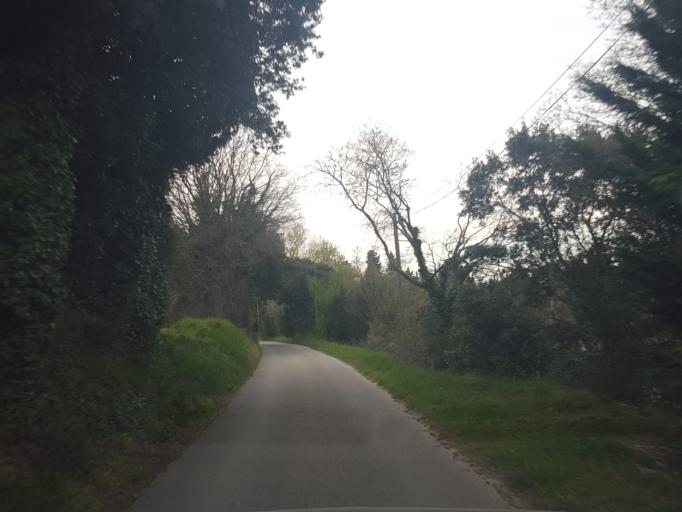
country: FR
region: Provence-Alpes-Cote d'Azur
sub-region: Departement du Vaucluse
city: Chateauneuf-de-Gadagne
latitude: 43.9349
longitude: 4.9445
